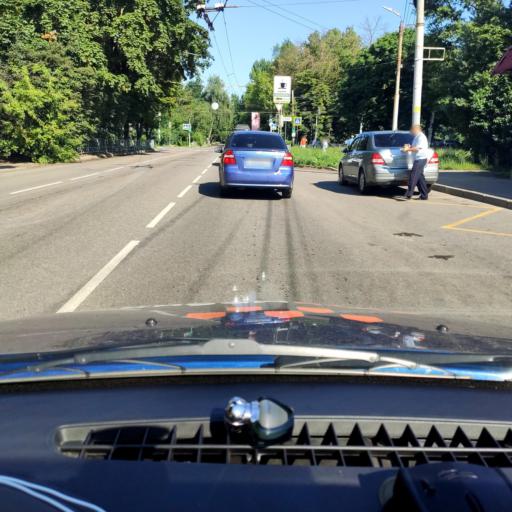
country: RU
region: Orjol
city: Orel
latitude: 52.9743
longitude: 36.0518
